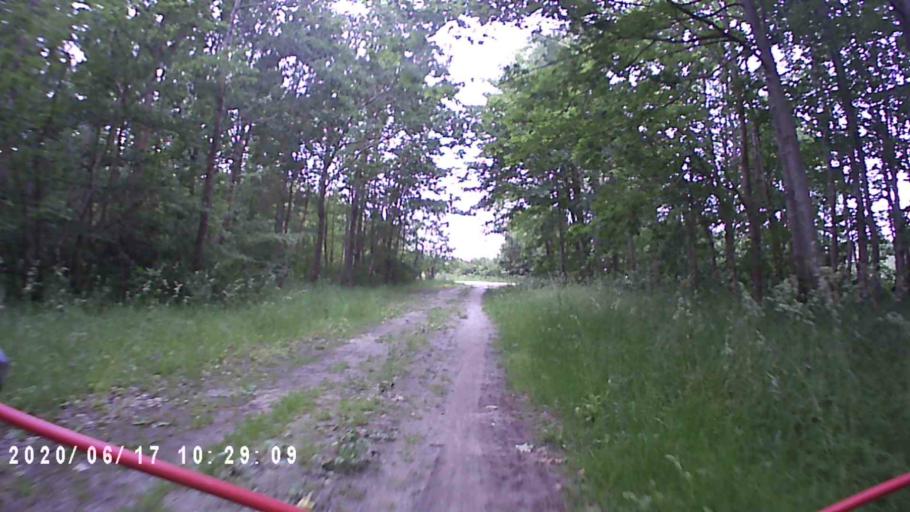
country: NL
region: Groningen
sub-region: Gemeente De Marne
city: Ulrum
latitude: 53.3964
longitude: 6.2399
